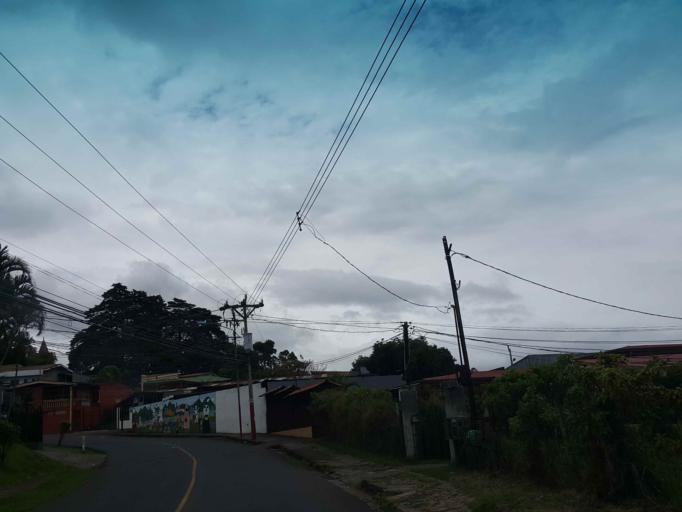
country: CR
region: Heredia
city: Heredia
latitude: 10.0088
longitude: -84.1197
